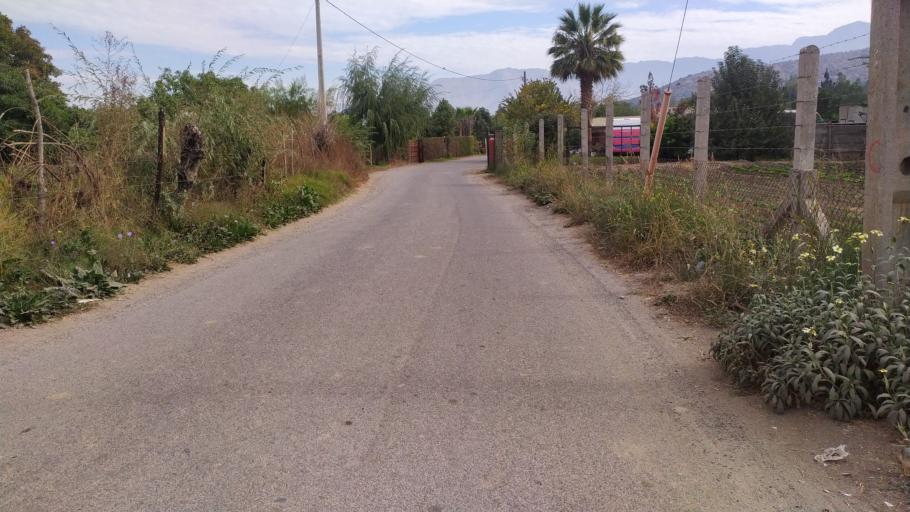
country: CL
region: Valparaiso
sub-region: Provincia de San Felipe
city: Llaillay
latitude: -32.7831
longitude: -70.9140
